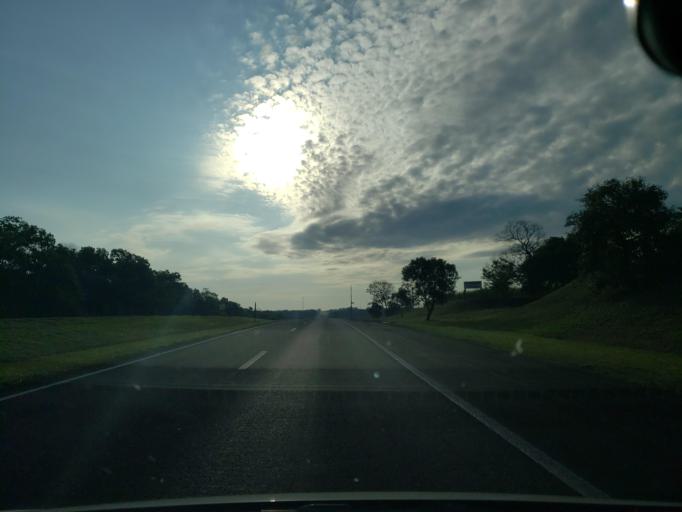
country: BR
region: Sao Paulo
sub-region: Valparaiso
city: Valparaiso
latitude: -21.1831
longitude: -50.9178
